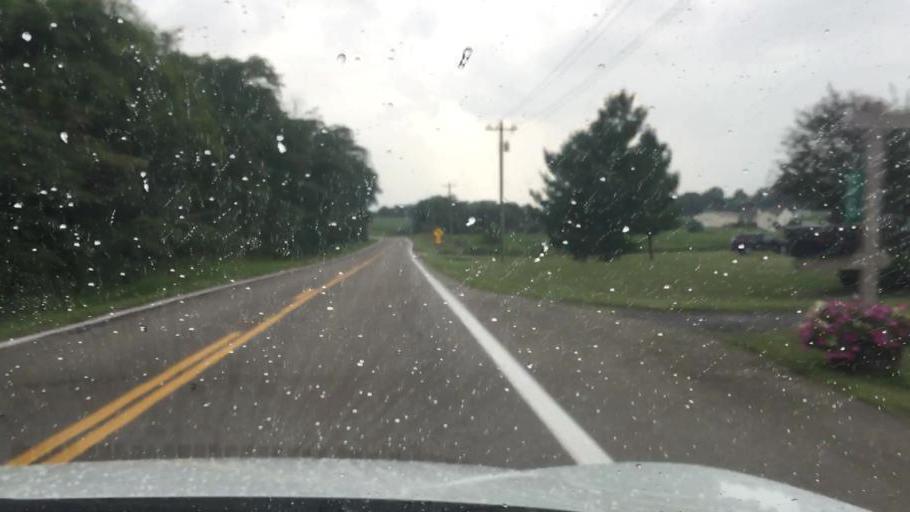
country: US
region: Ohio
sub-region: Champaign County
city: Mechanicsburg
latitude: 40.1003
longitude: -83.5668
